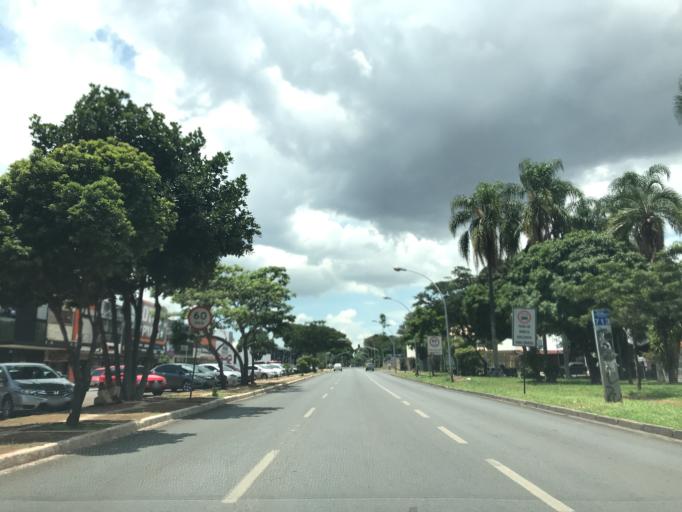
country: BR
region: Federal District
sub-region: Brasilia
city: Brasilia
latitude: -15.8206
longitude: -47.9177
